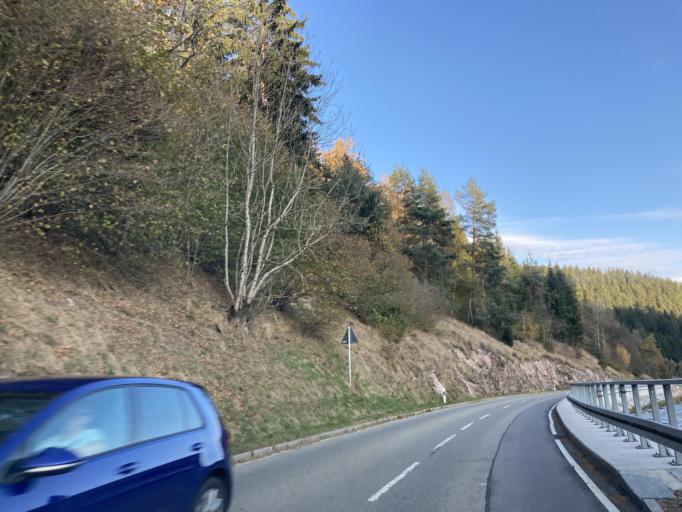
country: DE
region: Baden-Wuerttemberg
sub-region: Freiburg Region
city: Vohrenbach
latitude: 47.9947
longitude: 8.3467
